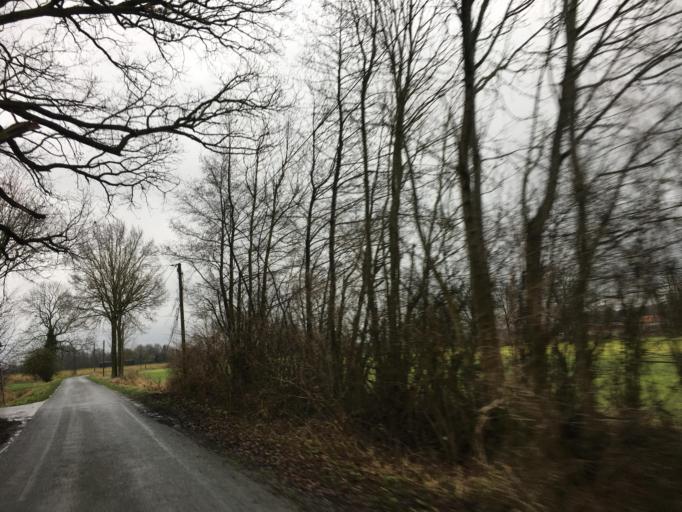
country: DE
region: North Rhine-Westphalia
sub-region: Regierungsbezirk Munster
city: Nordwalde
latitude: 52.0969
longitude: 7.5142
